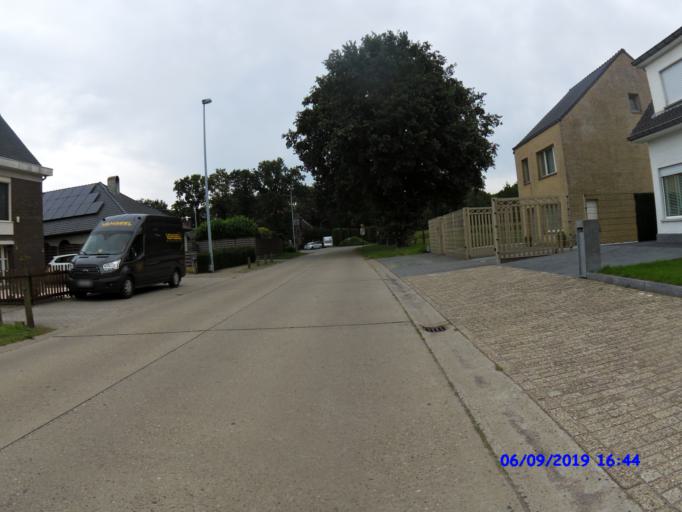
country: BE
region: Flanders
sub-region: Provincie Antwerpen
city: Turnhout
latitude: 51.2933
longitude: 4.9513
